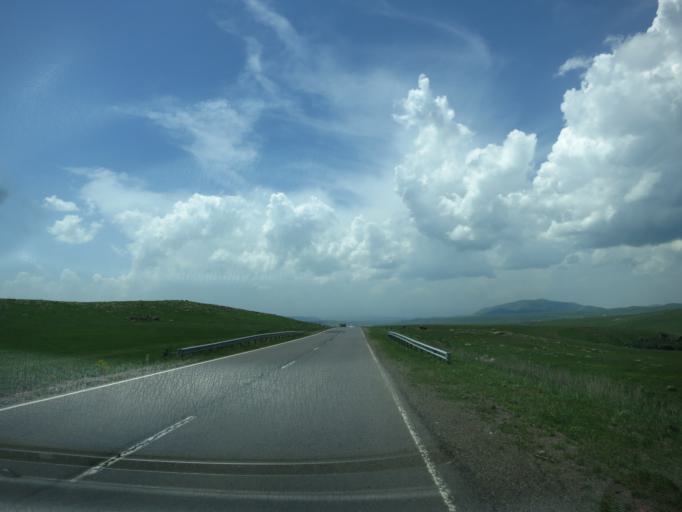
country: GE
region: Samtskhe-Javakheti
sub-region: Ninotsminda
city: Ninotsminda
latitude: 41.2919
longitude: 43.7132
